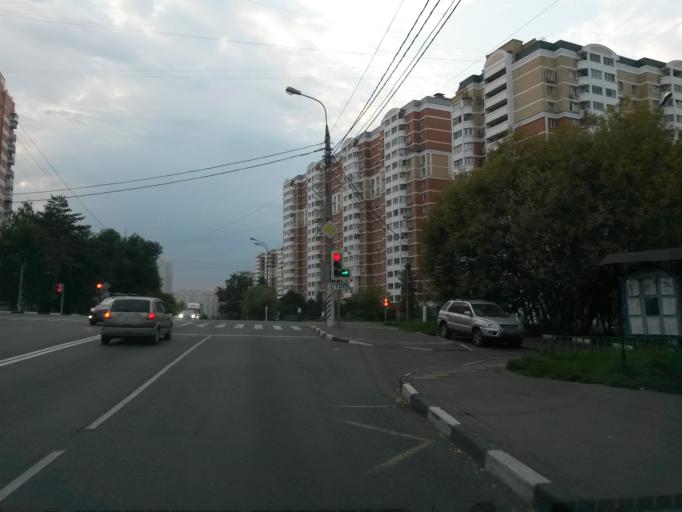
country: RU
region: Moscow
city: Annino
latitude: 55.5628
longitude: 37.5840
